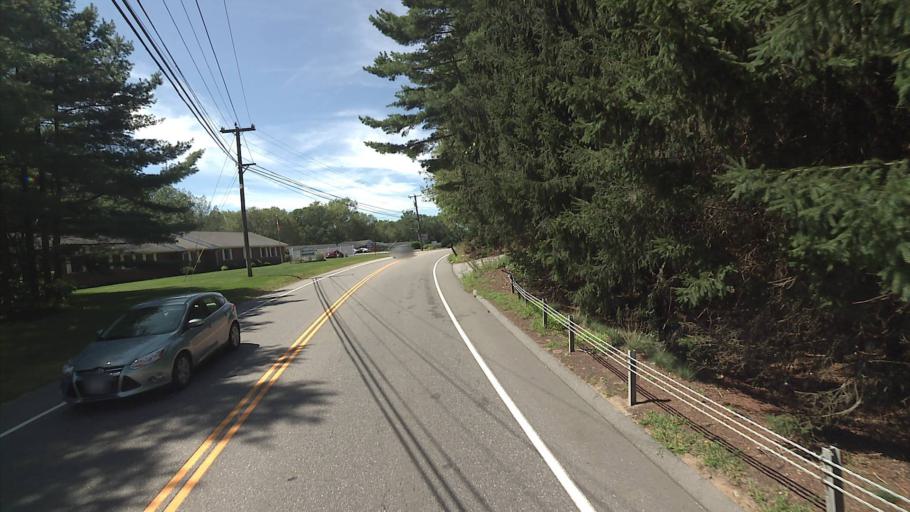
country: US
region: Connecticut
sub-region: Windham County
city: Killingly Center
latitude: 41.8385
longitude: -71.8702
